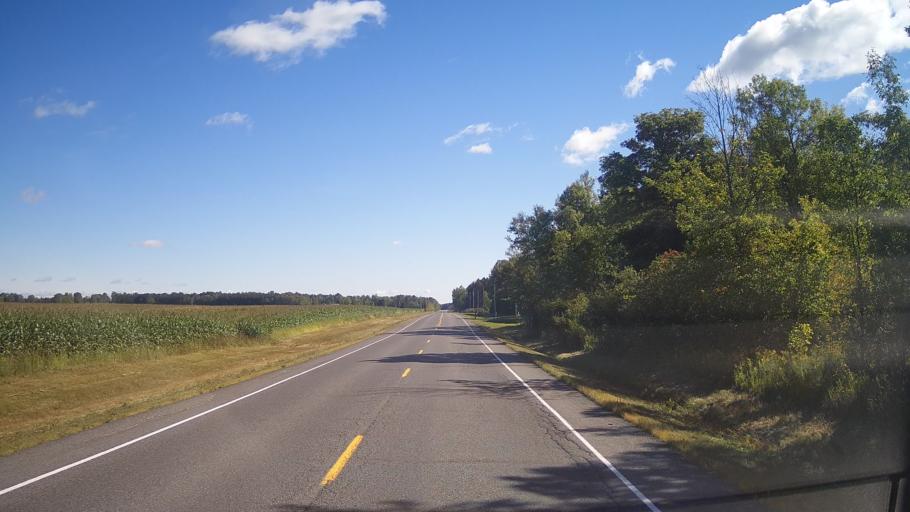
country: CA
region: Ontario
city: Prescott
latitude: 44.9084
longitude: -75.4332
